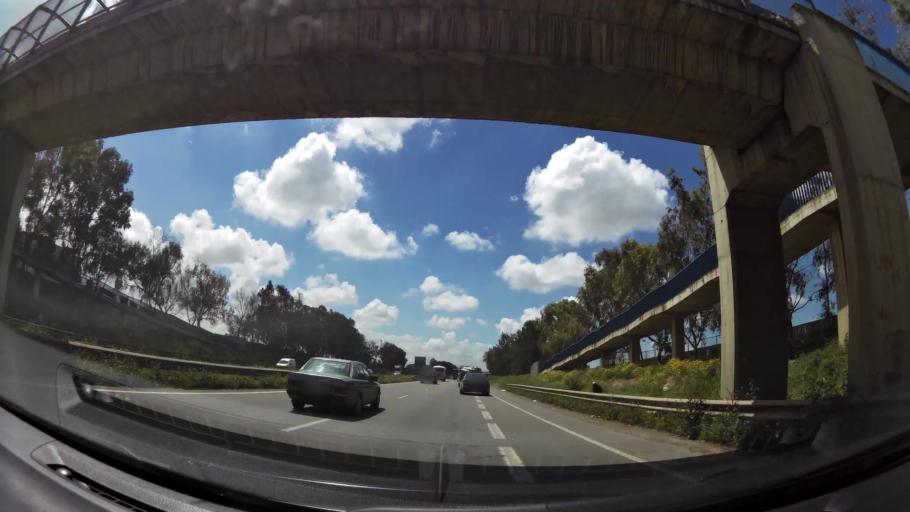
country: MA
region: Grand Casablanca
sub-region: Casablanca
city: Casablanca
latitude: 33.5216
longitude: -7.5769
